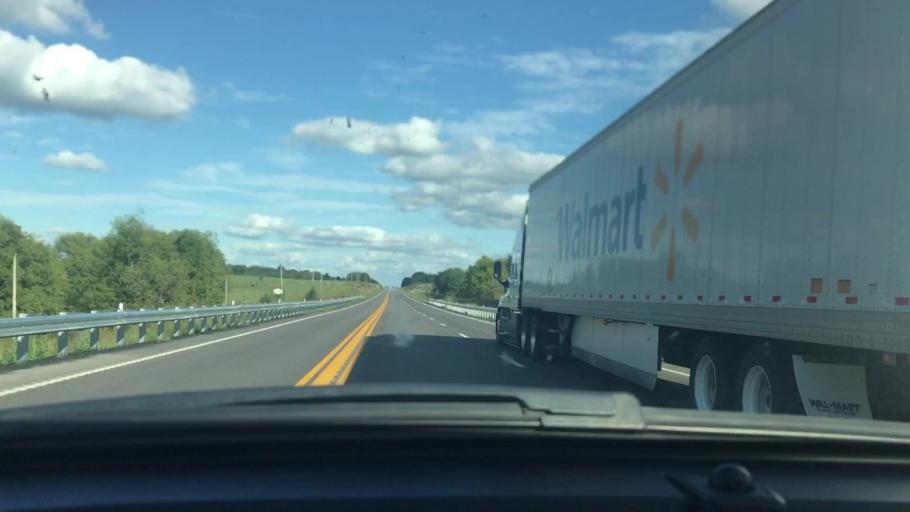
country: US
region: Missouri
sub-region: Oregon County
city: Thayer
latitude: 36.5864
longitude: -91.6265
